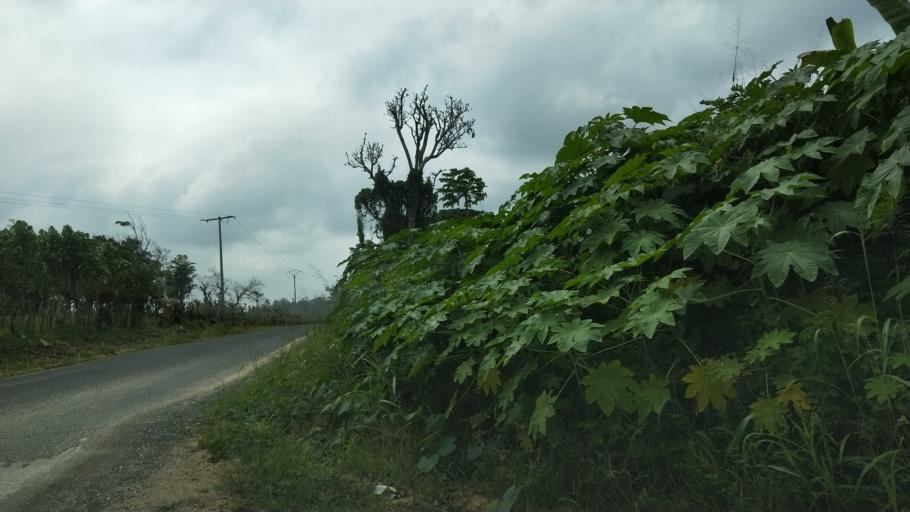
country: VU
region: Shefa
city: Port-Vila
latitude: -17.7666
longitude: 168.3772
